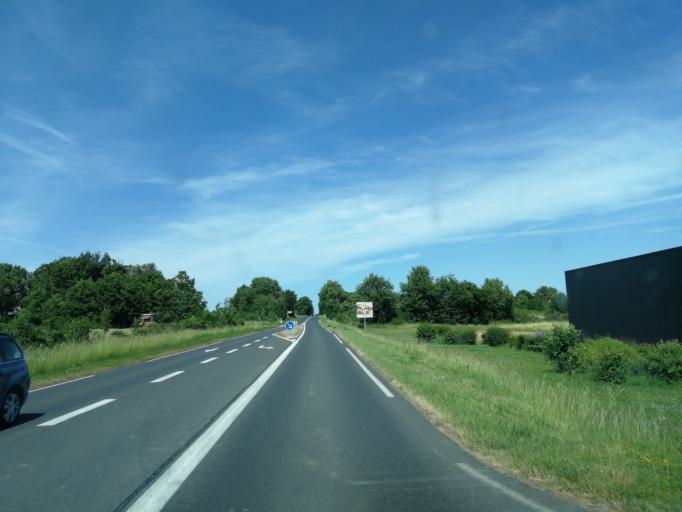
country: FR
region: Poitou-Charentes
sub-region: Departement des Deux-Sevres
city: Saint-Varent
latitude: 46.9051
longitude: -0.2846
